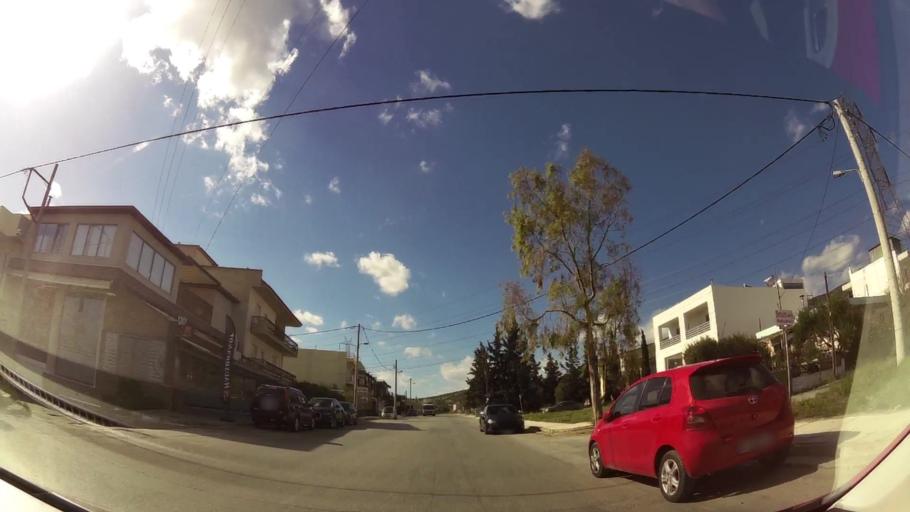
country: GR
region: Attica
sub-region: Nomarchia Anatolikis Attikis
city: Acharnes
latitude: 38.0979
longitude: 23.7263
